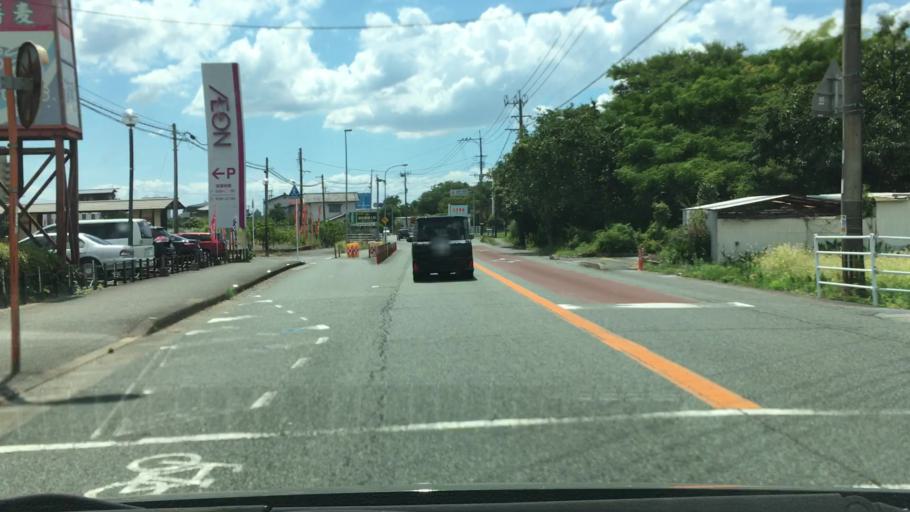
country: JP
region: Saga Prefecture
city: Kanzakimachi-kanzaki
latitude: 33.3352
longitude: 130.4171
